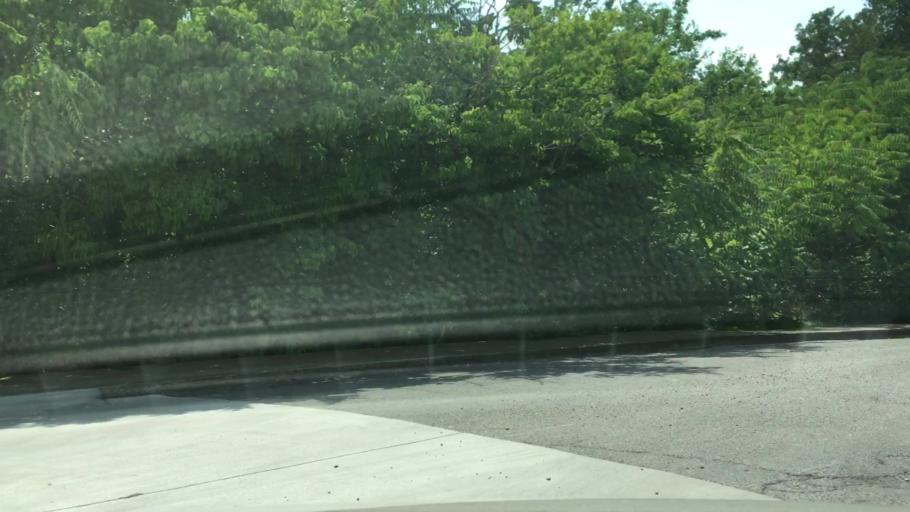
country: US
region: Oklahoma
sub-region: Cherokee County
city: Tahlequah
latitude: 35.9135
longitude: -94.9673
